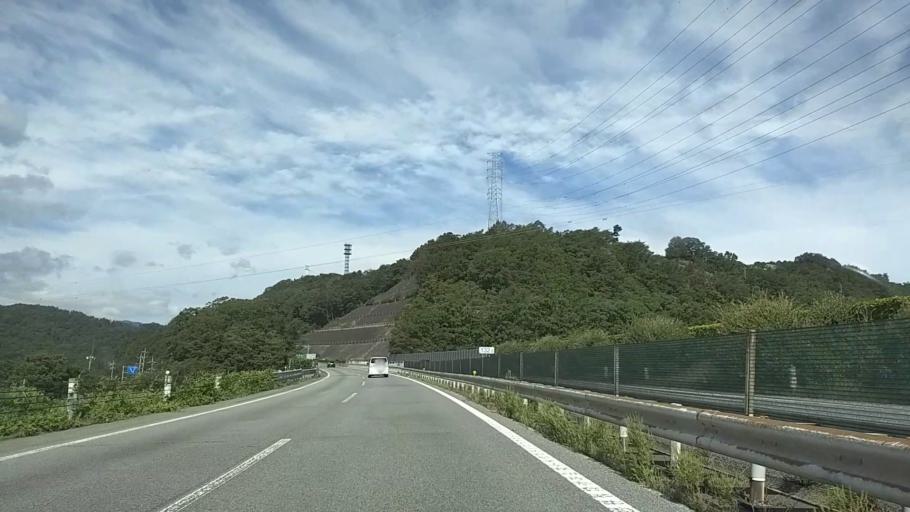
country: JP
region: Yamanashi
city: Nirasaki
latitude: 35.7840
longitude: 138.4192
